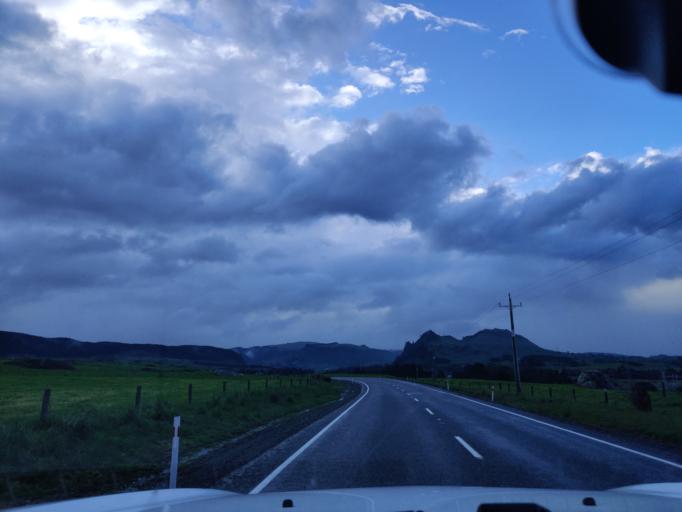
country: NZ
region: Waikato
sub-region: South Waikato District
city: Tokoroa
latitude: -38.4055
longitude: 175.7918
